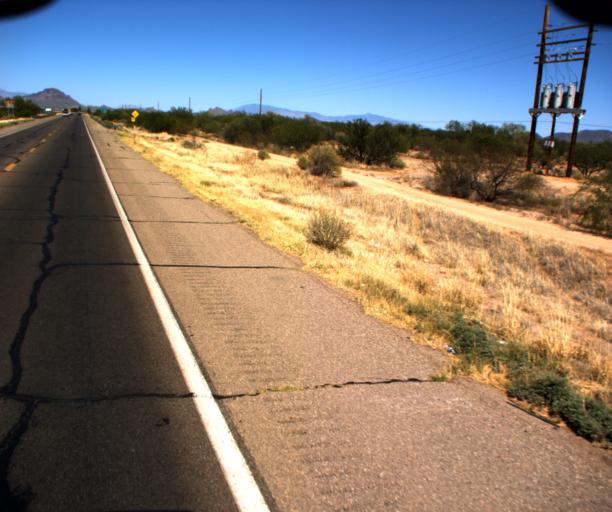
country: US
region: Arizona
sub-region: Pima County
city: Valencia West
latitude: 32.1288
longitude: -111.1863
